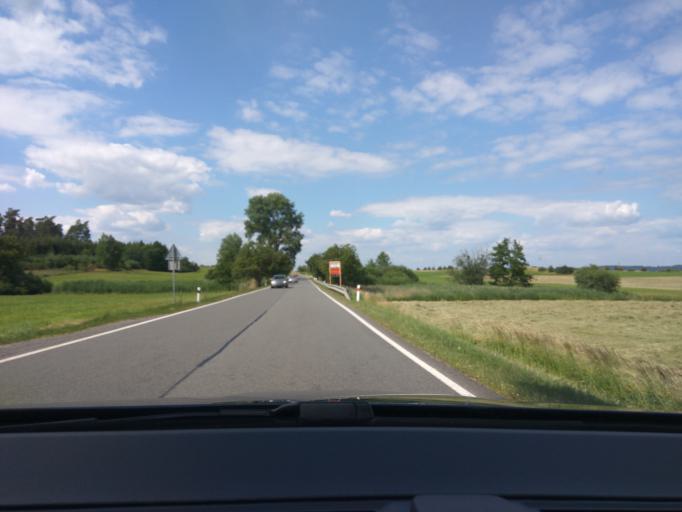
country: CZ
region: Jihocesky
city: Milevsko
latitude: 49.4283
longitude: 14.3593
